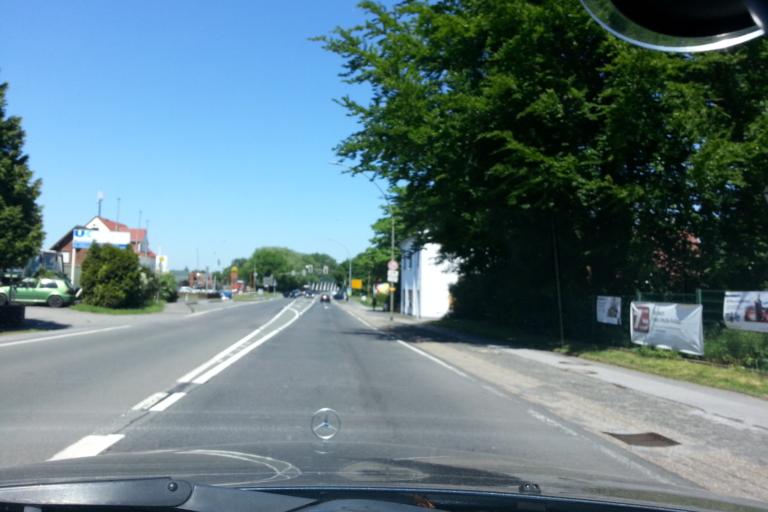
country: DE
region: North Rhine-Westphalia
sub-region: Regierungsbezirk Munster
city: Haltern
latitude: 51.7262
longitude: 7.1870
